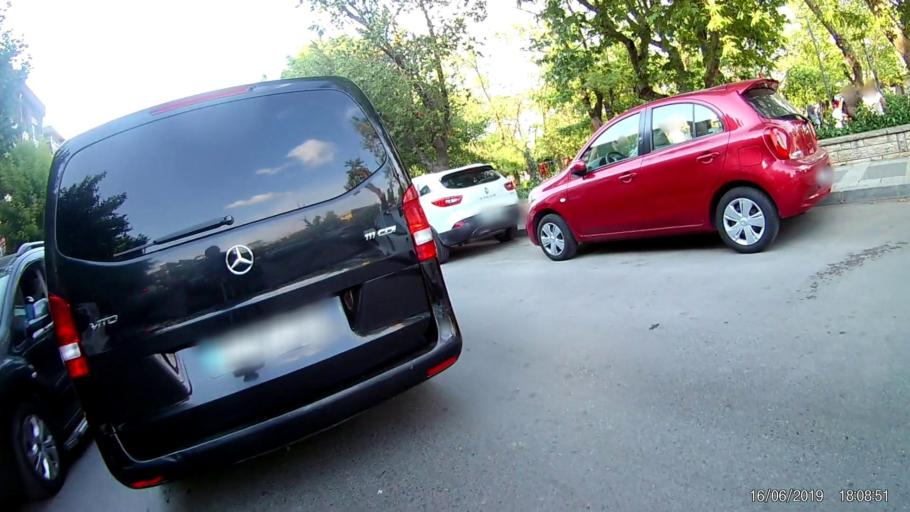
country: TR
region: Istanbul
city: UEskuedar
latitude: 40.9836
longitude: 29.0331
